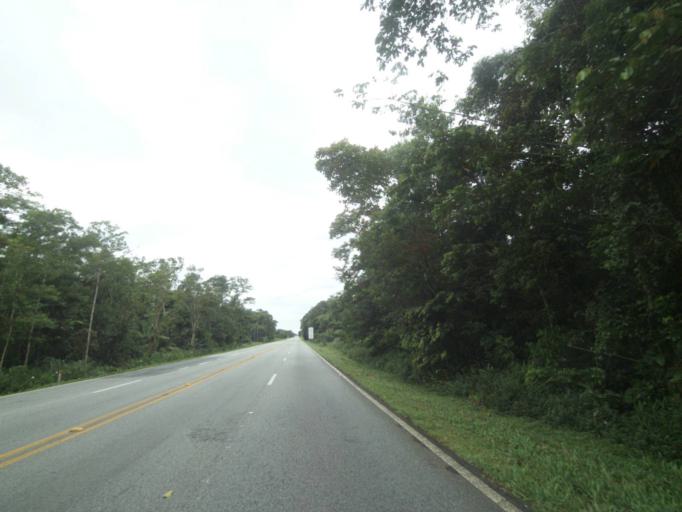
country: BR
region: Parana
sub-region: Pontal Do Parana
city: Pontal do Parana
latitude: -25.6409
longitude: -48.5915
